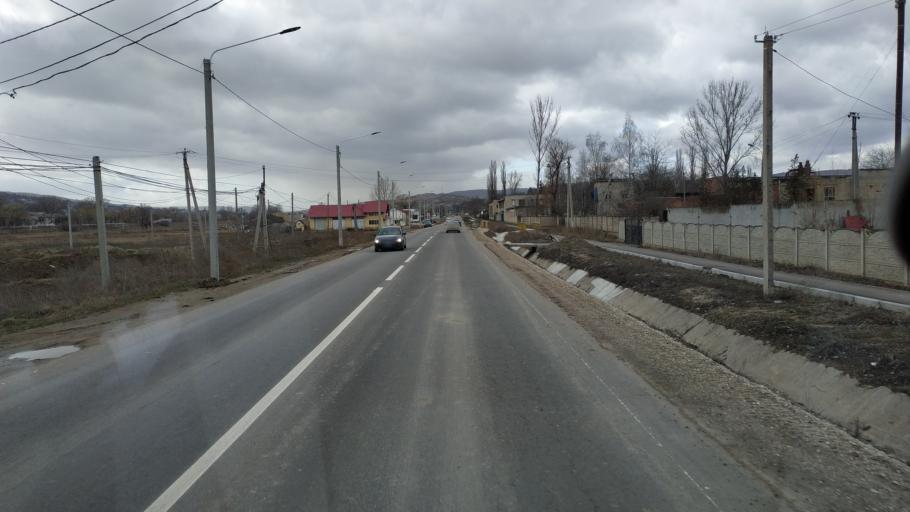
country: MD
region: Calarasi
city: Calarasi
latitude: 47.2791
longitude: 28.2111
